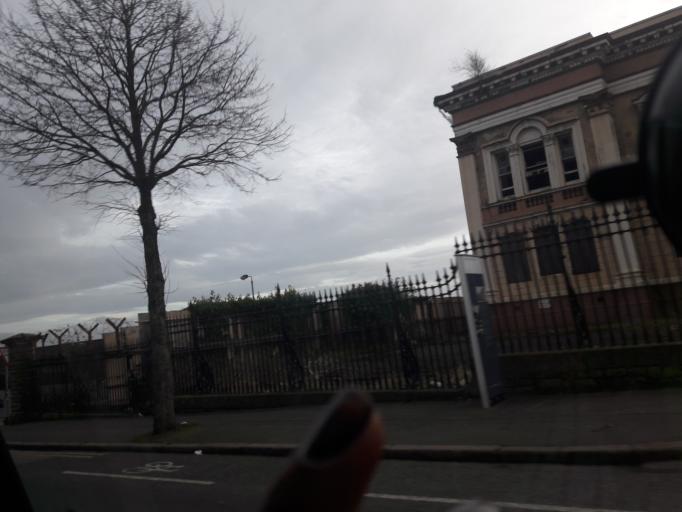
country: GB
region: Northern Ireland
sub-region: City of Belfast
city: Belfast
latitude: 54.6087
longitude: -5.9421
